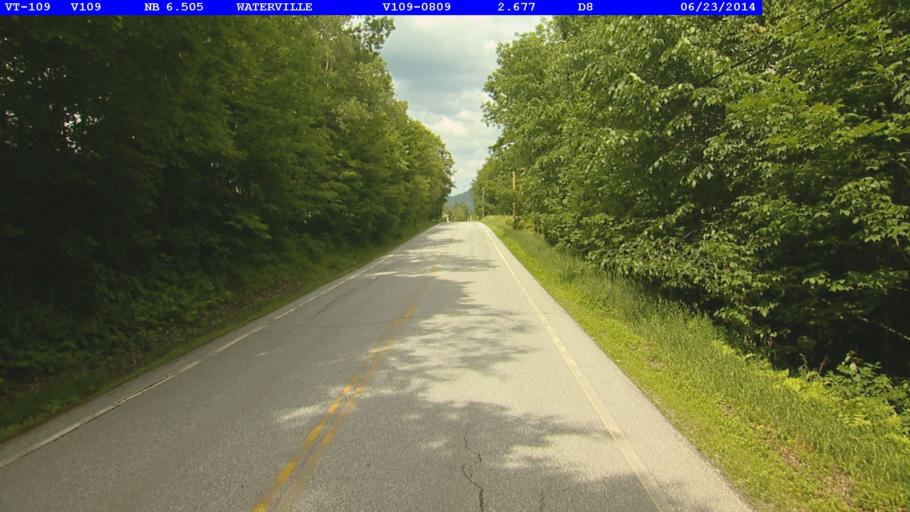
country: US
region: Vermont
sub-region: Lamoille County
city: Johnson
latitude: 44.7166
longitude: -72.7528
